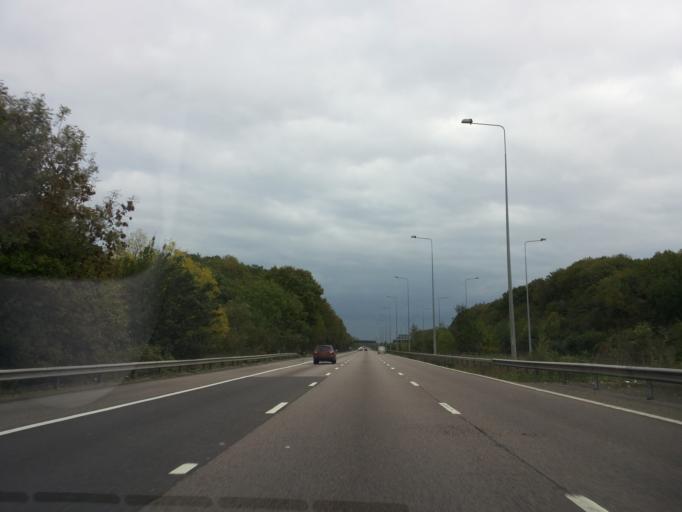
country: GB
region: England
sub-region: Kent
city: Boxley
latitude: 51.3264
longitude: 0.5313
